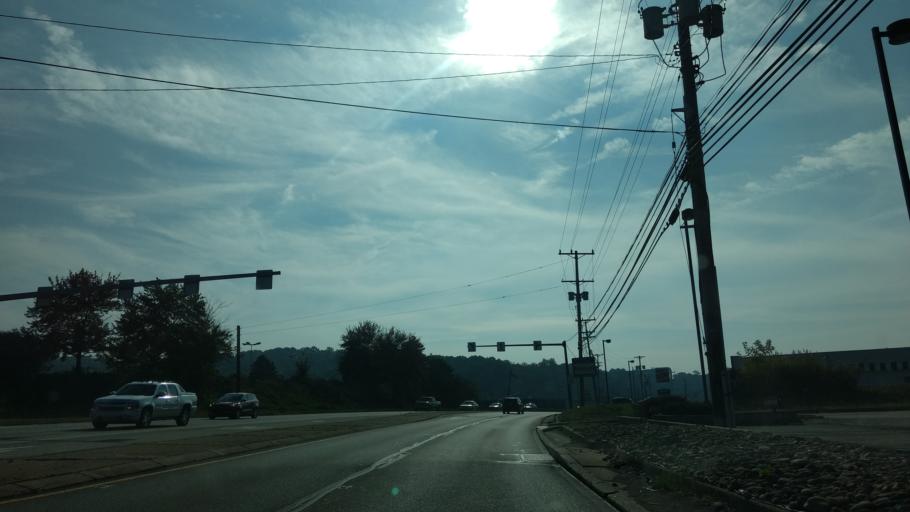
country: US
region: Pennsylvania
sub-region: Allegheny County
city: Pleasant Hills
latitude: 40.3366
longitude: -79.9487
